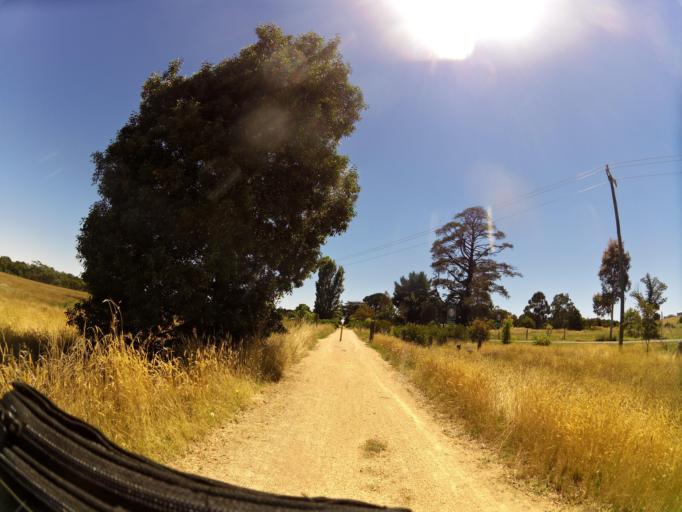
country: AU
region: Victoria
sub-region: Ballarat North
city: Delacombe
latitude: -37.6734
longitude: 143.6543
